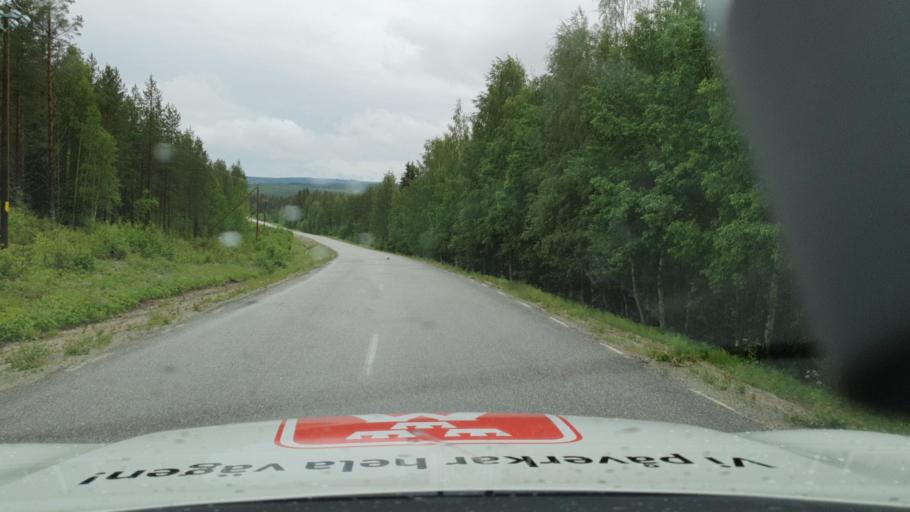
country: SE
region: Vaesterbotten
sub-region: Asele Kommun
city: Asele
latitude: 63.9971
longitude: 17.1726
